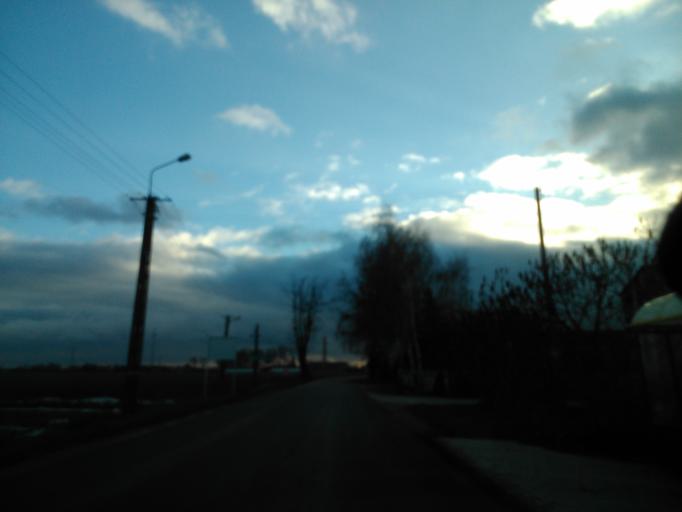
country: PL
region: Masovian Voivodeship
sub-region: Powiat warszawski zachodni
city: Blonie
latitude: 52.2164
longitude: 20.6528
